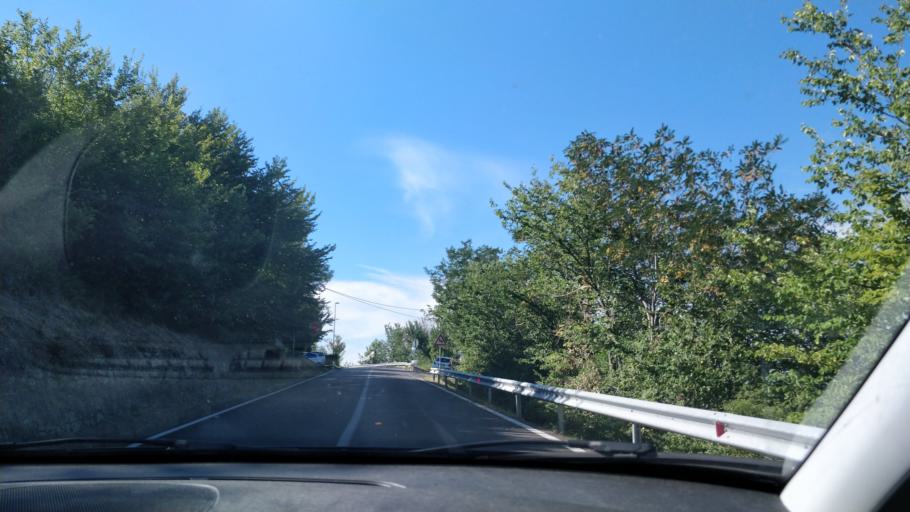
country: IT
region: Abruzzo
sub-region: Provincia di Pescara
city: Serramonacesca
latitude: 42.2551
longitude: 14.0905
